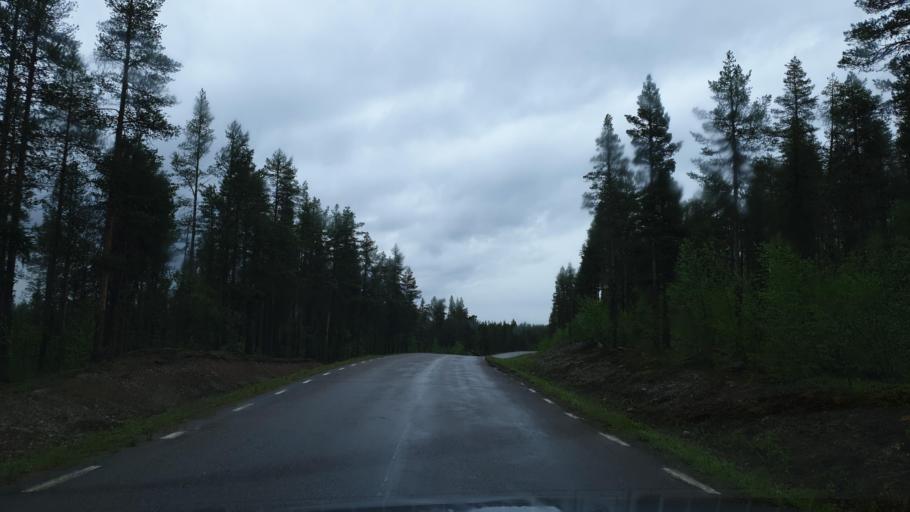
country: SE
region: Norrbotten
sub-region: Gallivare Kommun
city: Malmberget
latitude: 67.8908
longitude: 21.0429
